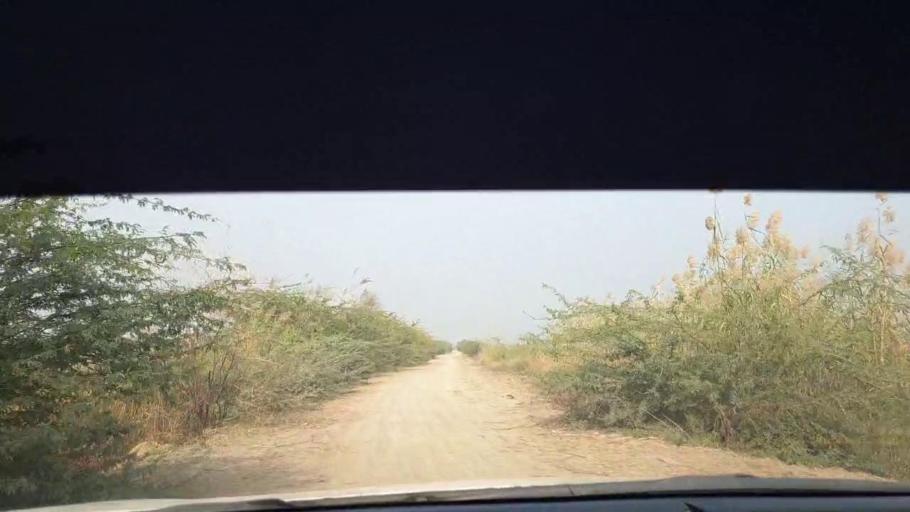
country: PK
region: Sindh
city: Berani
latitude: 25.8237
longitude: 68.8356
